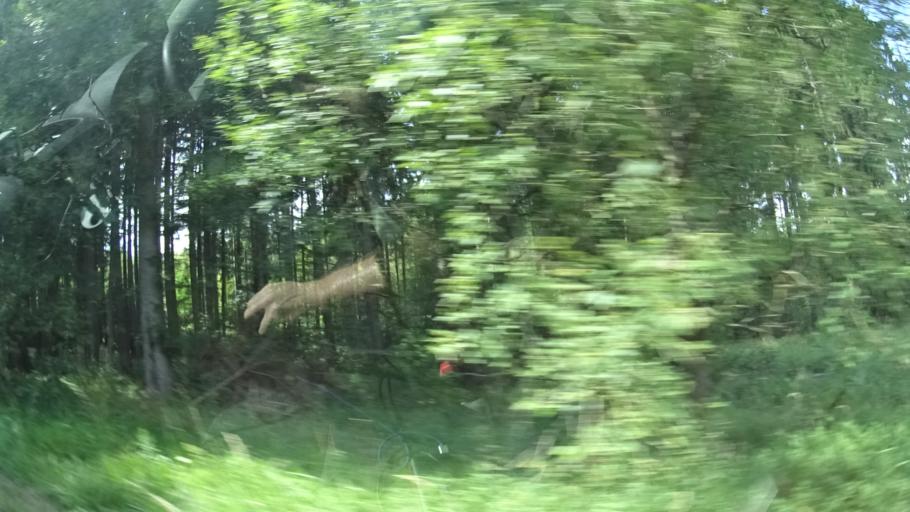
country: DE
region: Thuringia
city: Veilsdorf
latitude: 50.3938
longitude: 10.7821
